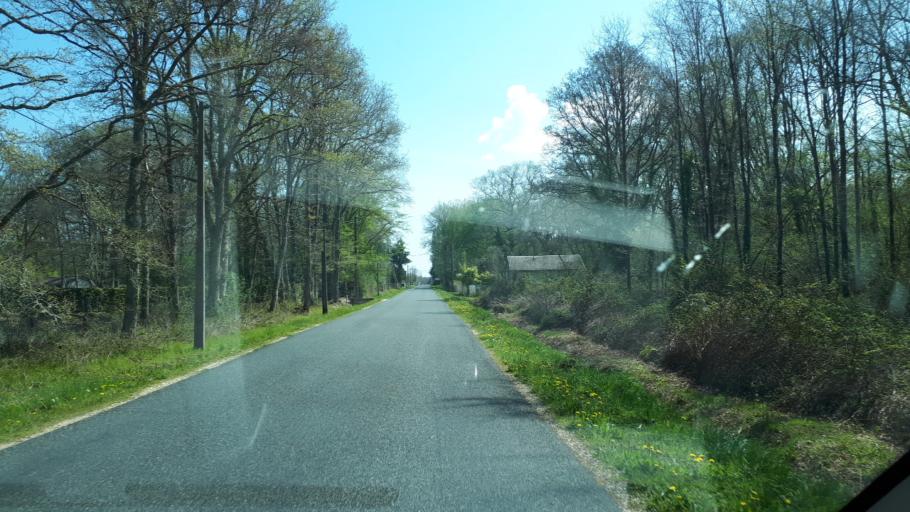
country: FR
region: Centre
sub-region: Departement du Cher
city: Neuvy-sur-Barangeon
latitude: 47.3165
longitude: 2.2447
